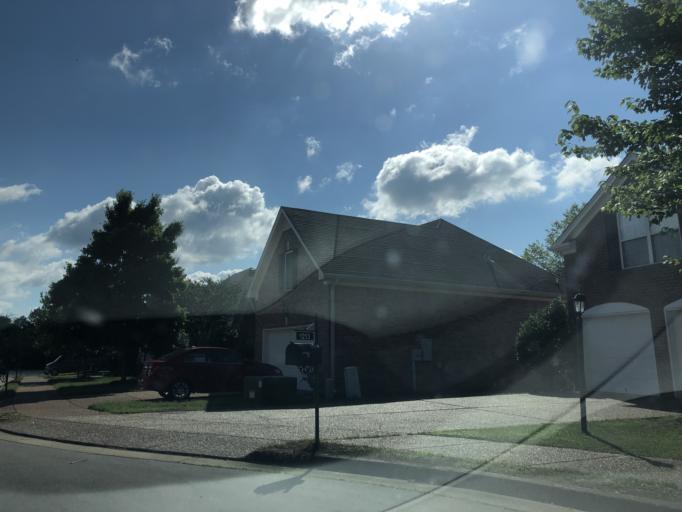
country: US
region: Tennessee
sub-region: Davidson County
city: Belle Meade
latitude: 36.0602
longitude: -86.9500
